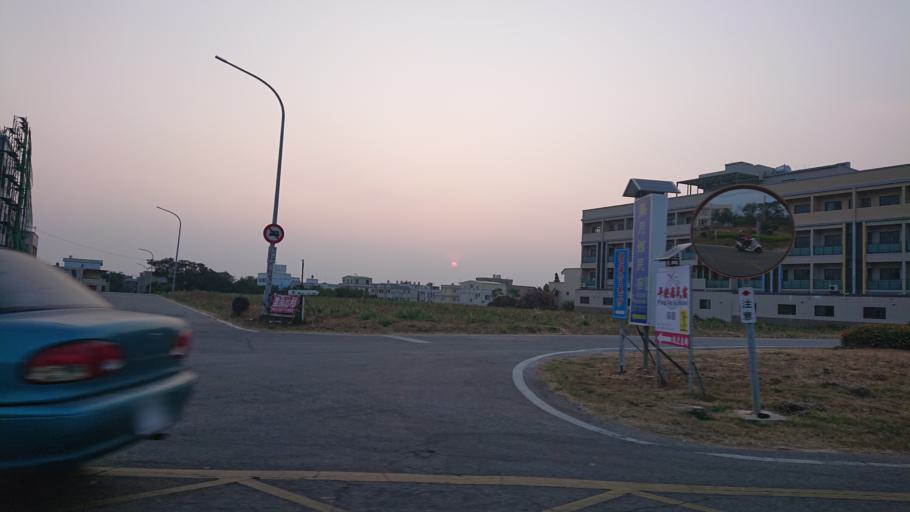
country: TW
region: Fukien
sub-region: Kinmen
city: Jincheng
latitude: 24.4450
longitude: 118.3194
